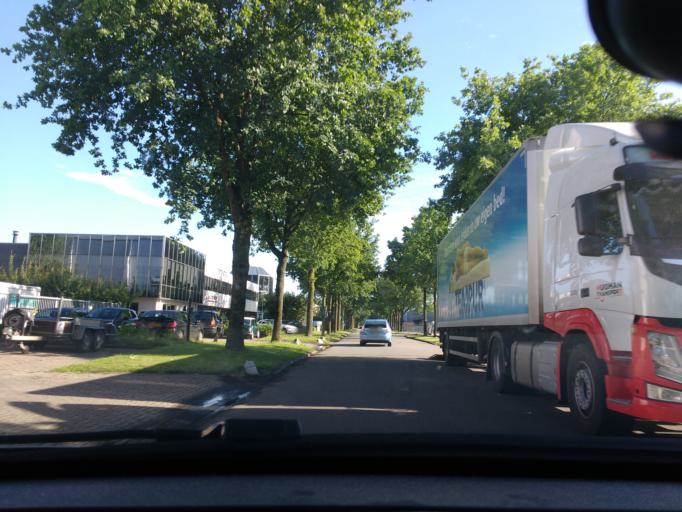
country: NL
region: Utrecht
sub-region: Gemeente Veenendaal
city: Veenendaal
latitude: 52.0388
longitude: 5.5410
